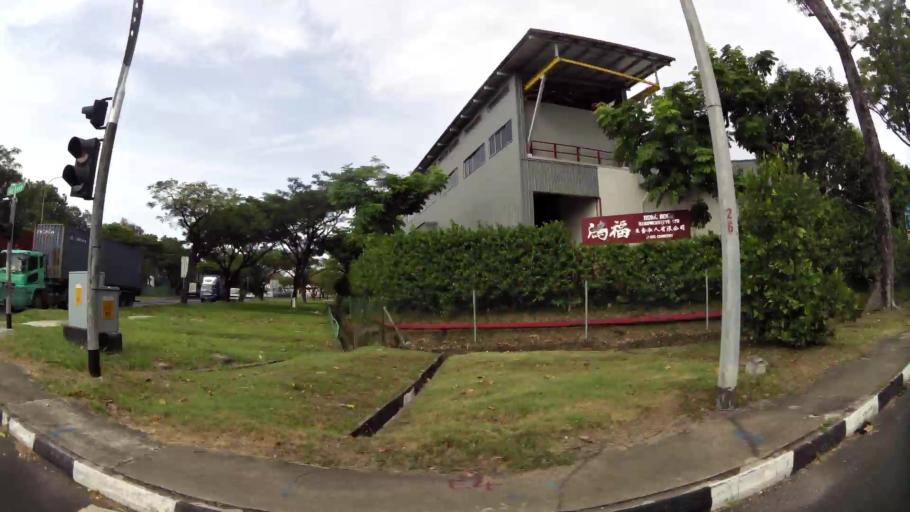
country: MY
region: Johor
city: Johor Bahru
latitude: 1.3082
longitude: 103.6653
